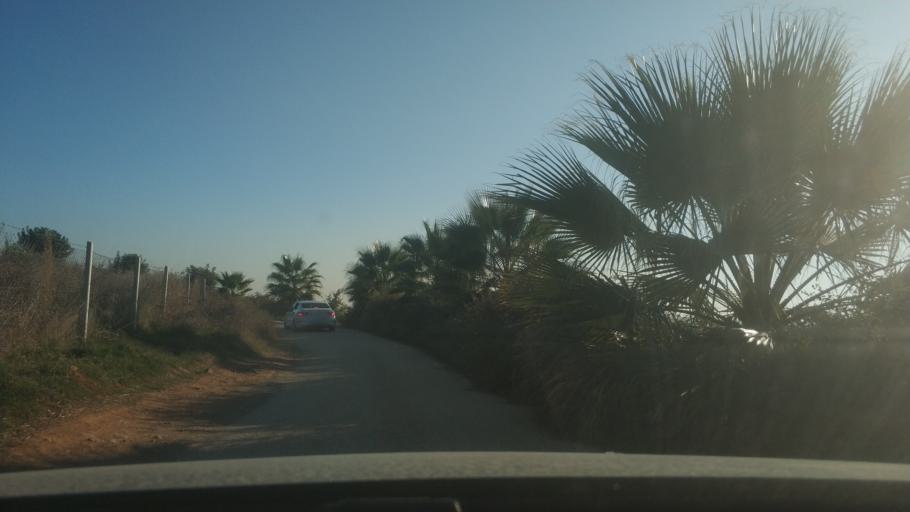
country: TR
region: Adana
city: Adana
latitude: 37.0906
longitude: 35.3012
